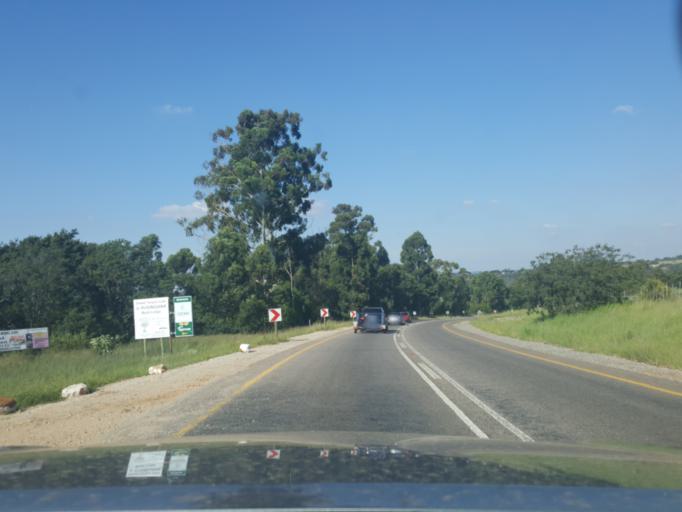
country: ZA
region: Gauteng
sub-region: City of Tshwane Metropolitan Municipality
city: Cullinan
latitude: -25.7762
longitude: 28.4843
